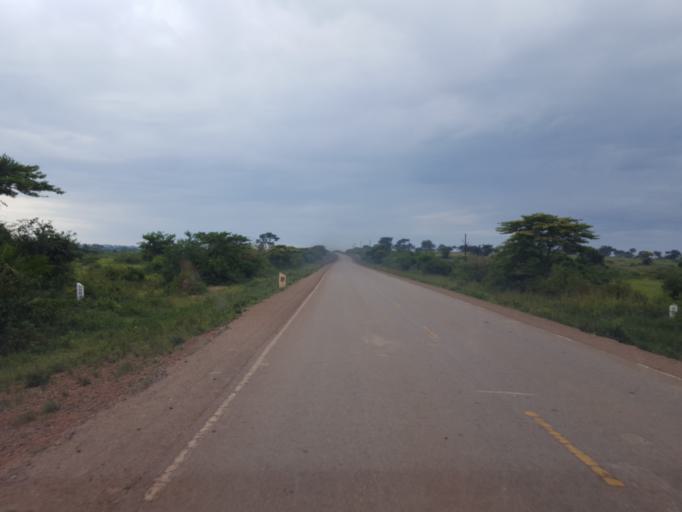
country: UG
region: Central Region
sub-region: Kyankwanzi District
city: Kyankwanzi
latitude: 1.1034
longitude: 31.6185
